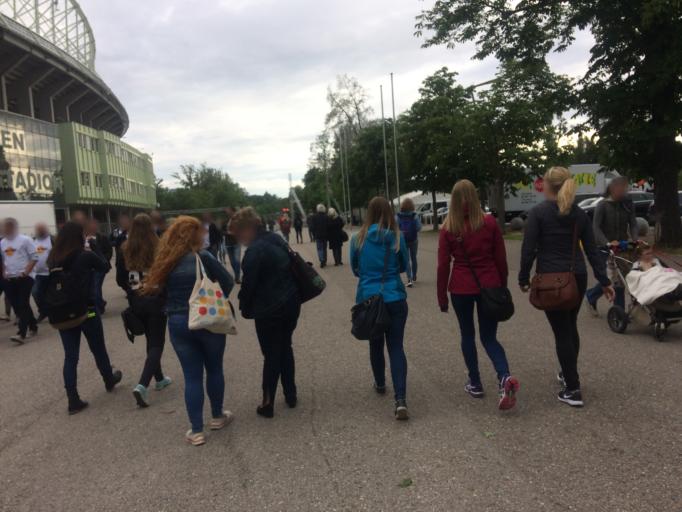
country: AT
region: Vienna
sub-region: Wien Stadt
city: Vienna
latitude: 48.2084
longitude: 16.4197
